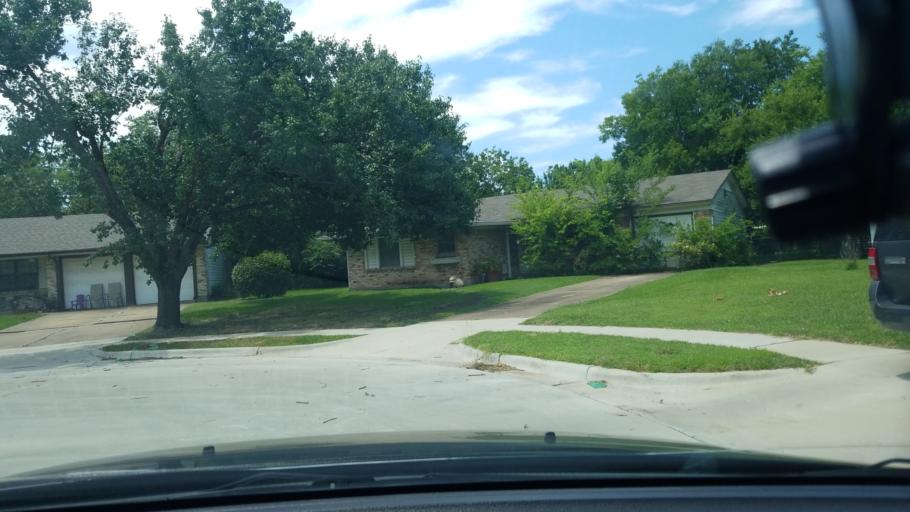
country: US
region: Texas
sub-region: Dallas County
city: Mesquite
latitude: 32.8033
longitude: -96.6505
